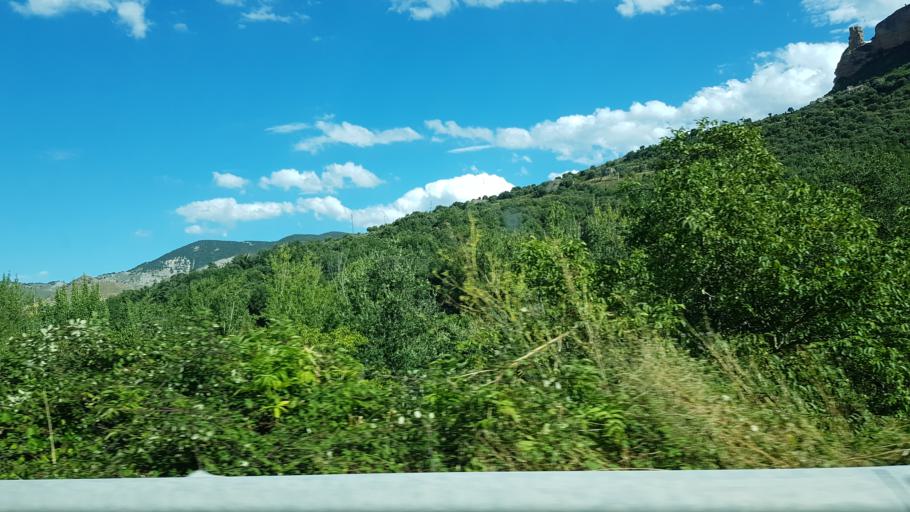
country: ES
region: La Rioja
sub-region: Provincia de La Rioja
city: Viguera
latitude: 42.3085
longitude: -2.5561
